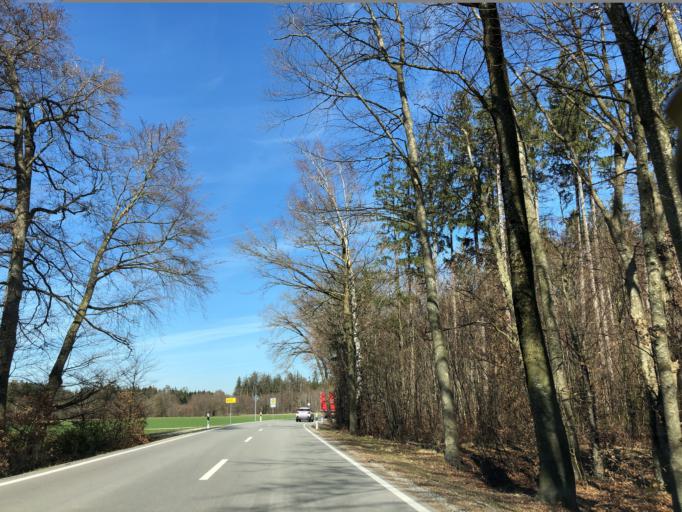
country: DE
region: Bavaria
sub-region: Upper Bavaria
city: Pfaffing
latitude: 48.0693
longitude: 12.1078
